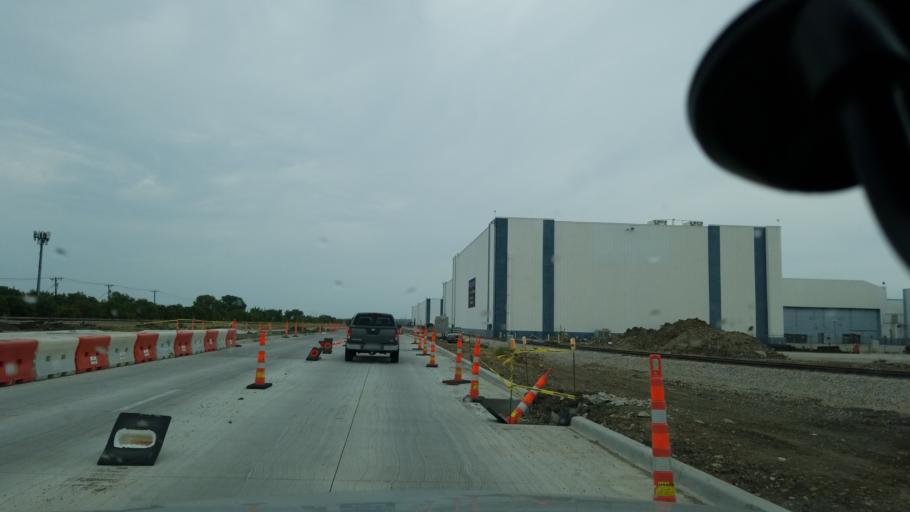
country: US
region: Texas
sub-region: Dallas County
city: Grand Prairie
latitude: 32.7451
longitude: -96.9864
